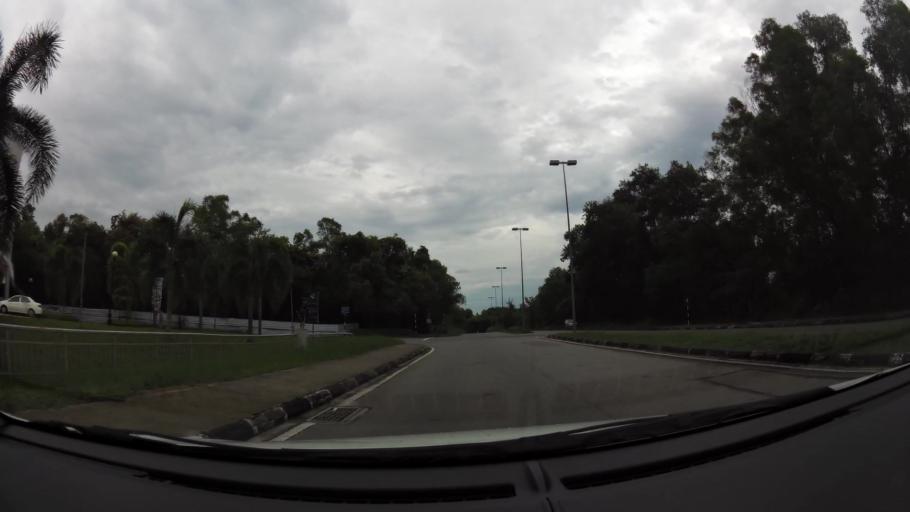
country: BN
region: Brunei and Muara
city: Bandar Seri Begawan
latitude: 4.9045
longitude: 114.9262
